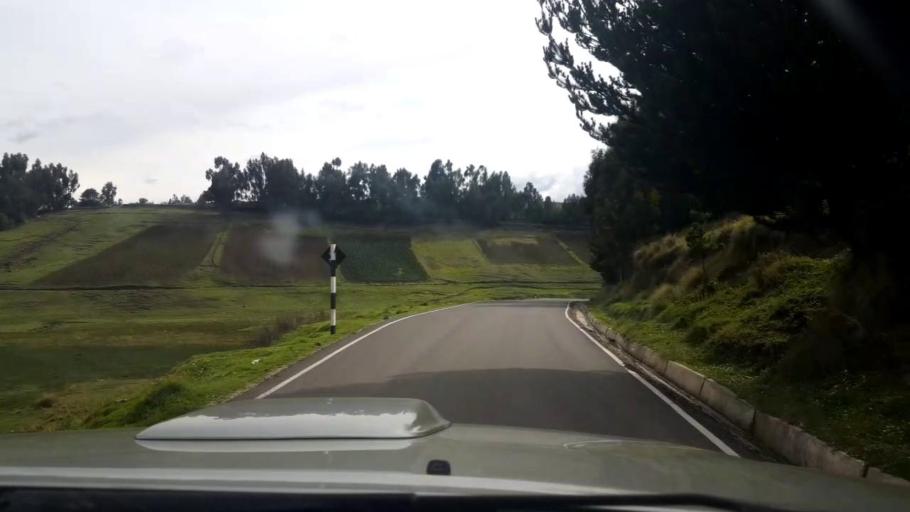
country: PE
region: Ayacucho
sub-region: Provincia de Cangallo
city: Pampa Cangallo
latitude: -13.4502
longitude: -74.2027
